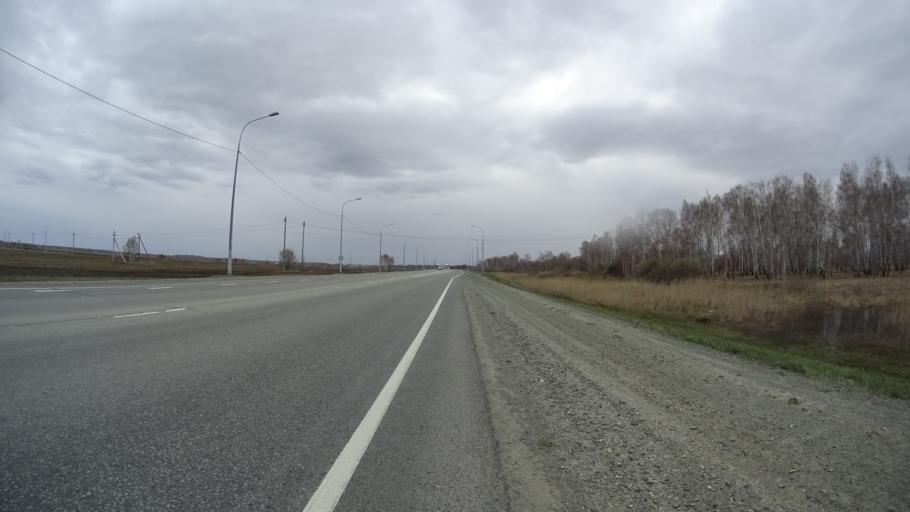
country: RU
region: Chelyabinsk
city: Krasnogorskiy
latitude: 54.6857
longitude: 61.2476
